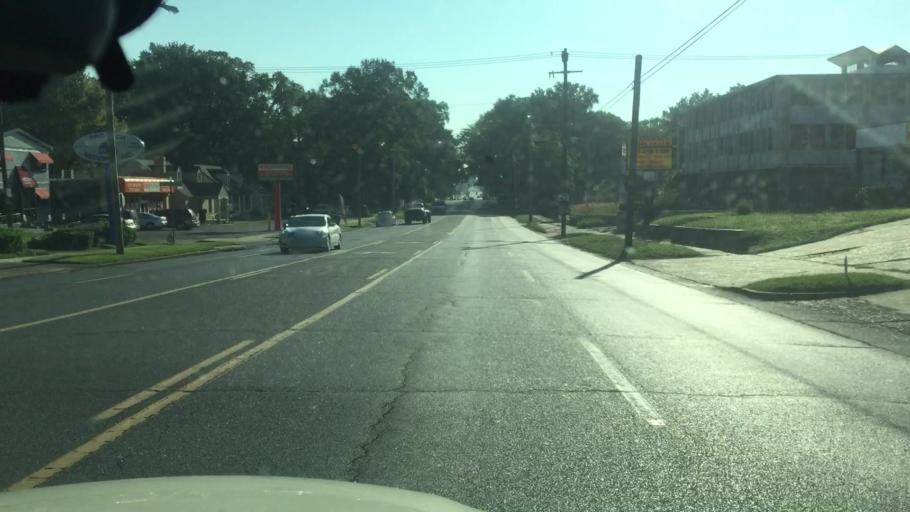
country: US
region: Tennessee
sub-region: Shelby County
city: Memphis
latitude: 35.1078
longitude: -89.9421
